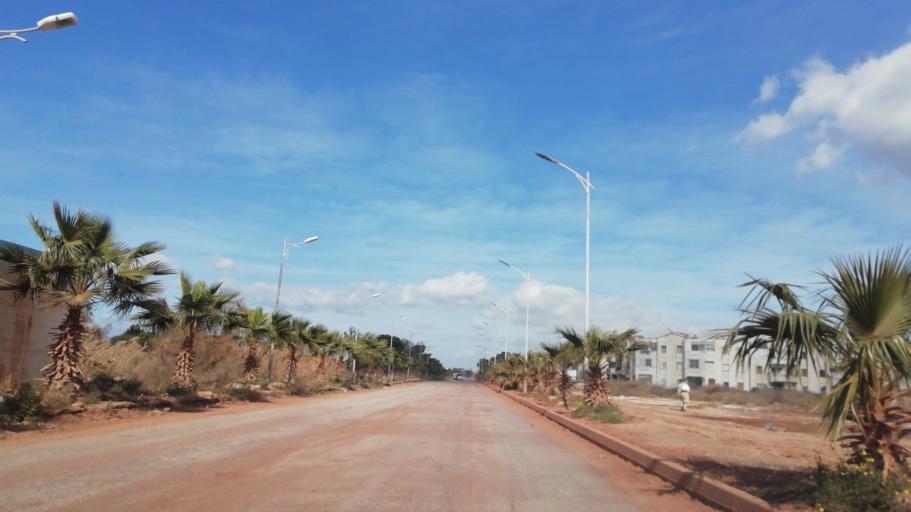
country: DZ
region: Oran
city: Es Senia
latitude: 35.6297
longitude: -0.5843
